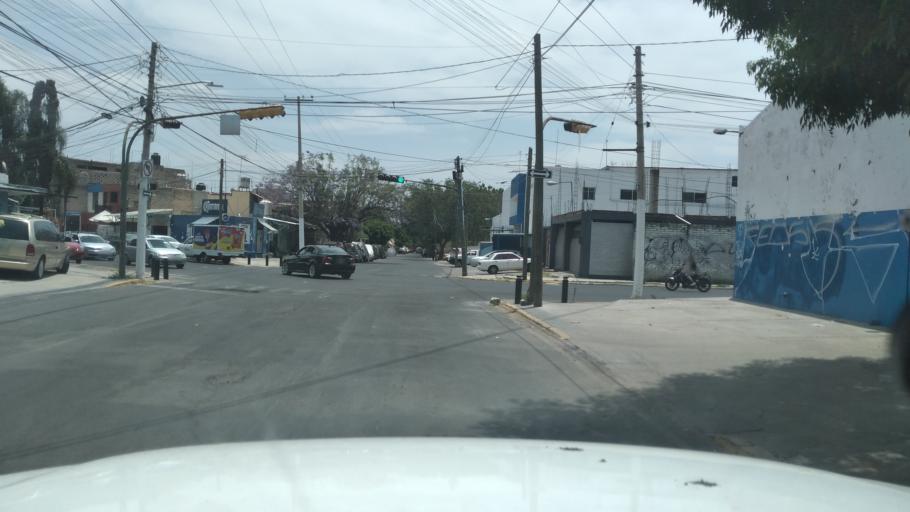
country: MX
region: Jalisco
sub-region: Zapopan
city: Zapopan
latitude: 20.7315
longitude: -103.3708
